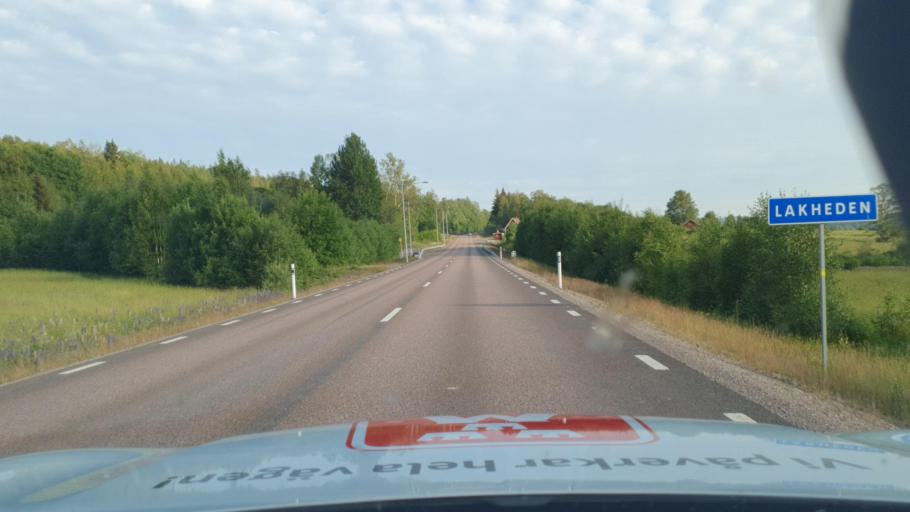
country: SE
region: Vaermland
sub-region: Hagfors Kommun
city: Hagfors
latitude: 59.9750
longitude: 13.6563
